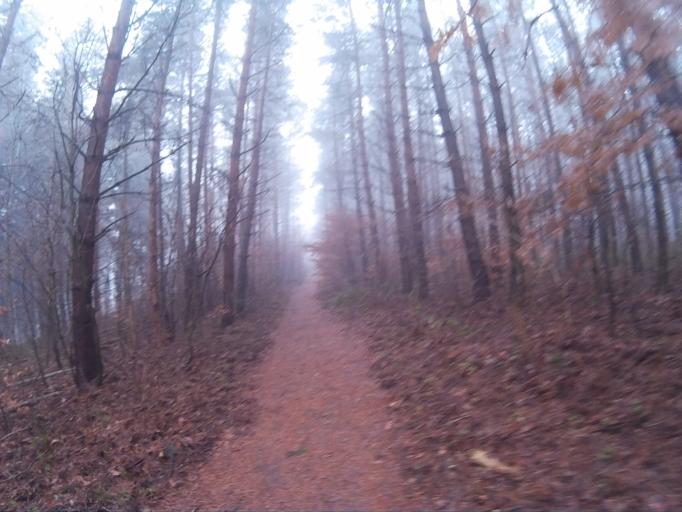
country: HU
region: Nograd
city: Somoskoujfalu
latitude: 48.1422
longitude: 19.8495
